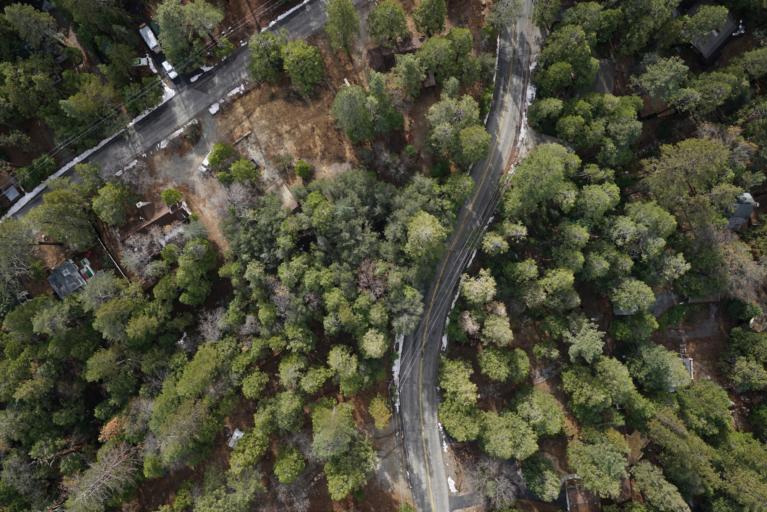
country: US
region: California
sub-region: Riverside County
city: Idyllwild
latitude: 33.7477
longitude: -116.7041
